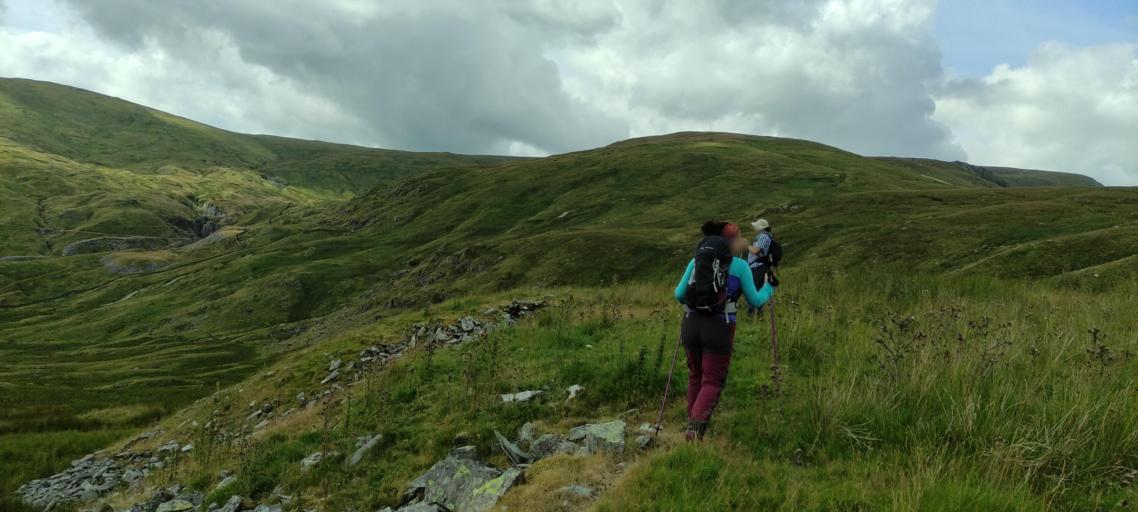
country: GB
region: England
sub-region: Cumbria
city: Windermere
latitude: 54.4732
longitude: -2.8013
